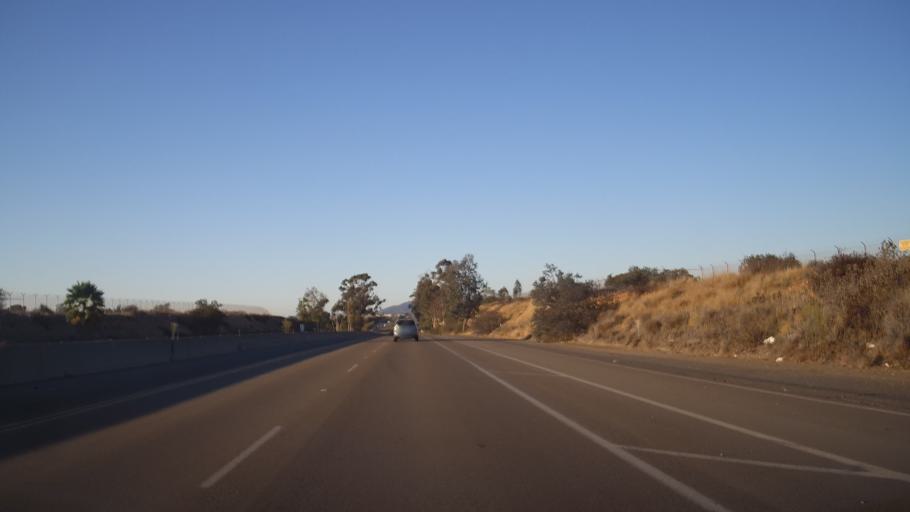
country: US
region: California
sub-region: San Diego County
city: Poway
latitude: 32.8653
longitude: -117.1165
